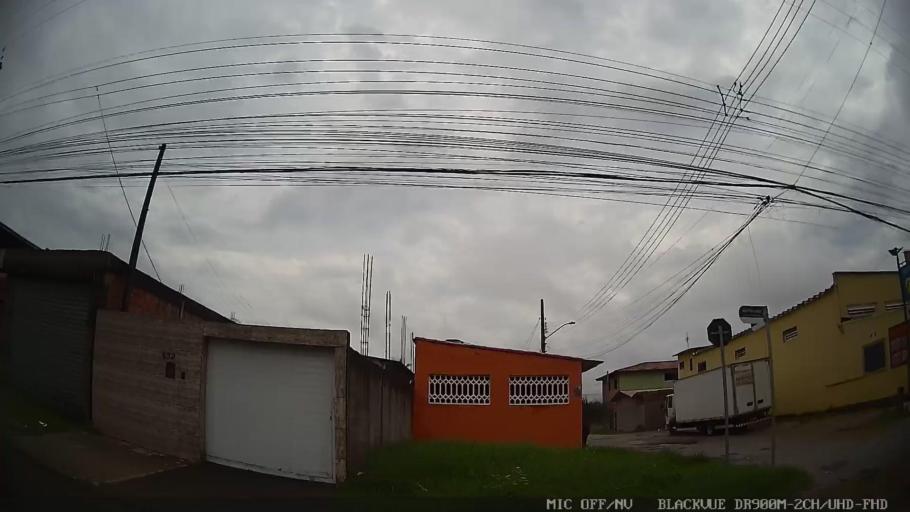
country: BR
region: Sao Paulo
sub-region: Sao Sebastiao
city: Sao Sebastiao
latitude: -23.7051
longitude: -45.4472
